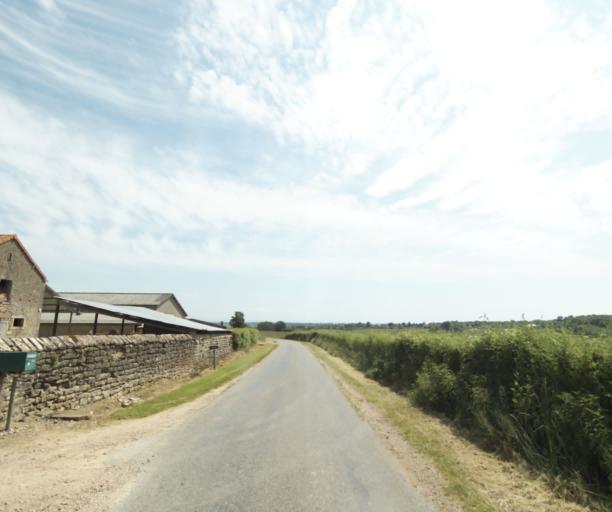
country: FR
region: Bourgogne
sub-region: Departement de Saone-et-Loire
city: Perrecy-les-Forges
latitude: 46.5859
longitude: 4.1405
